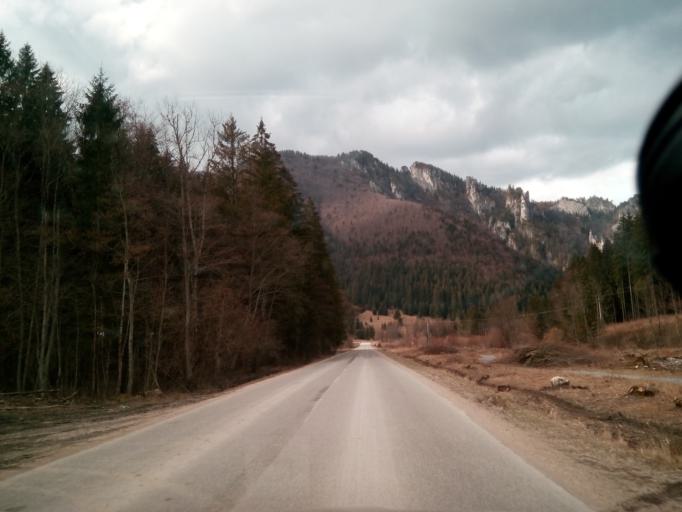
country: SK
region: Zilinsky
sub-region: Okres Zilina
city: Terchova
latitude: 49.2341
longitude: 19.0477
